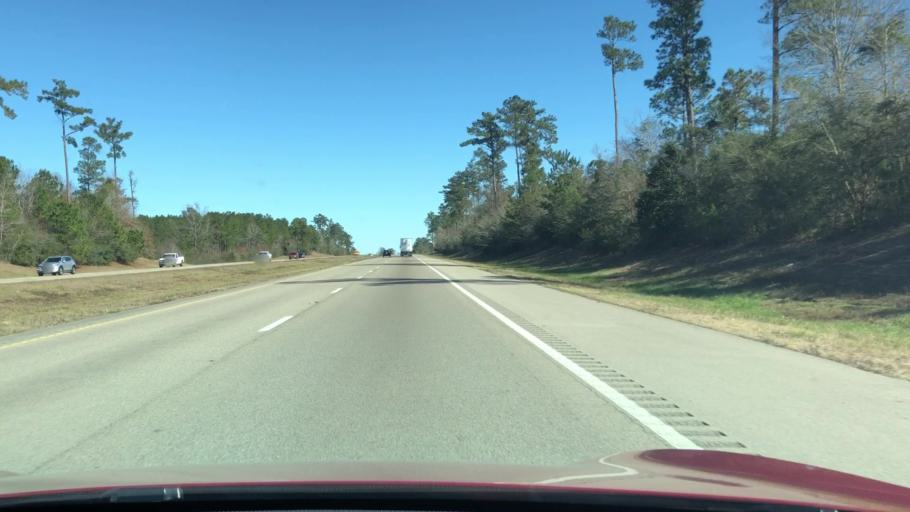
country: US
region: Mississippi
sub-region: Pearl River County
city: Poplarville
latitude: 30.7399
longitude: -89.5342
